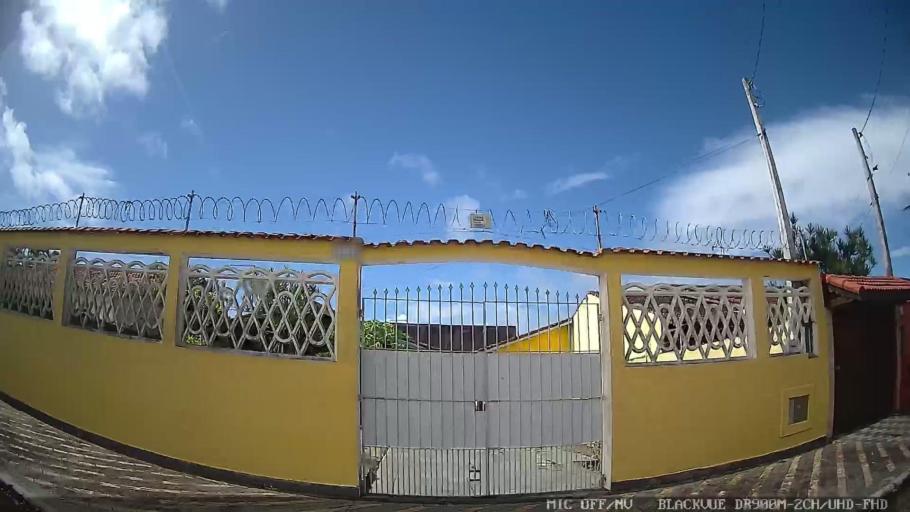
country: BR
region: Sao Paulo
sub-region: Itanhaem
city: Itanhaem
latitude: -24.2448
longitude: -46.8914
